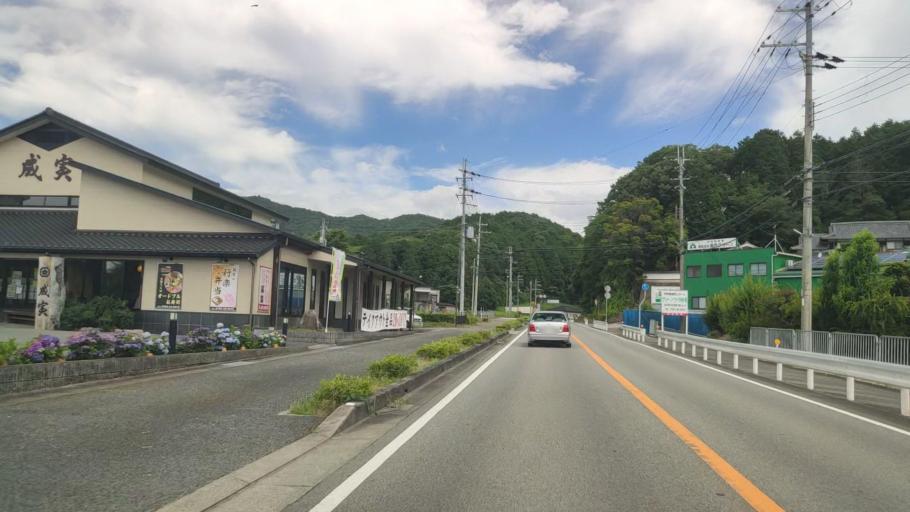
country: JP
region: Hyogo
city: Nishiwaki
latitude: 35.0527
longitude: 134.9184
